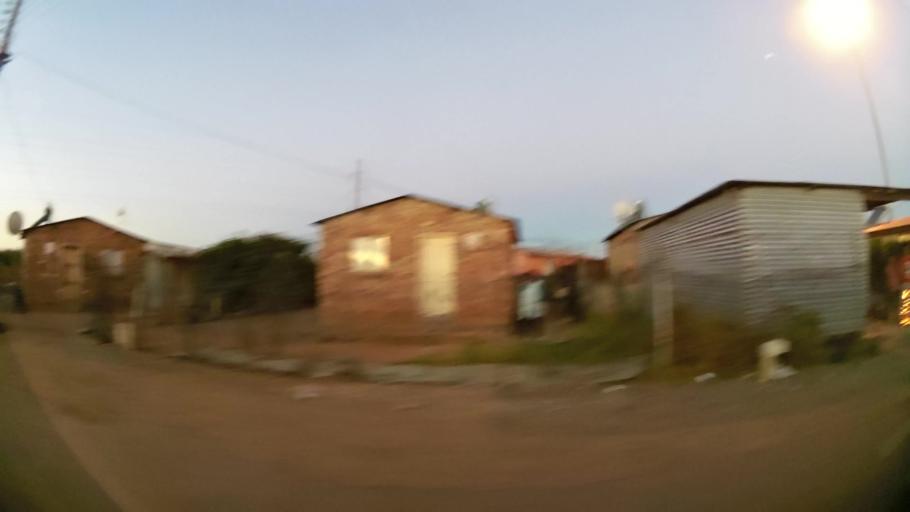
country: ZA
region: Northern Cape
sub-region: Frances Baard District Municipality
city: Kimberley
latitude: -28.7117
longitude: 24.7571
